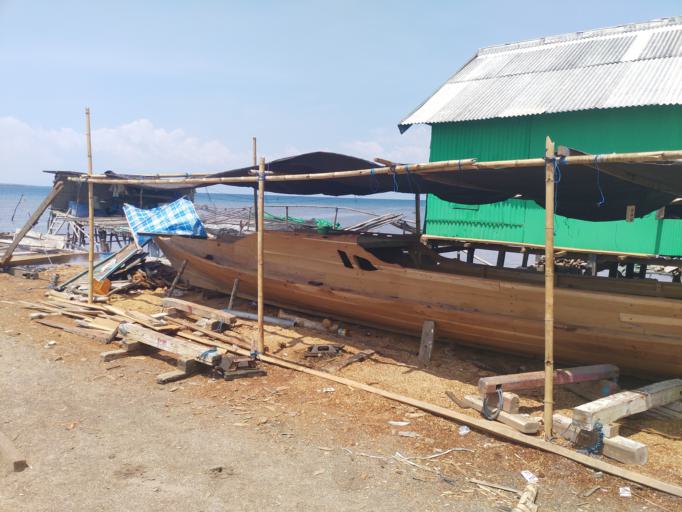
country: ID
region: West Nusa Tenggara
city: Labuhanjambu
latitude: -8.6946
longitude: 118.0200
